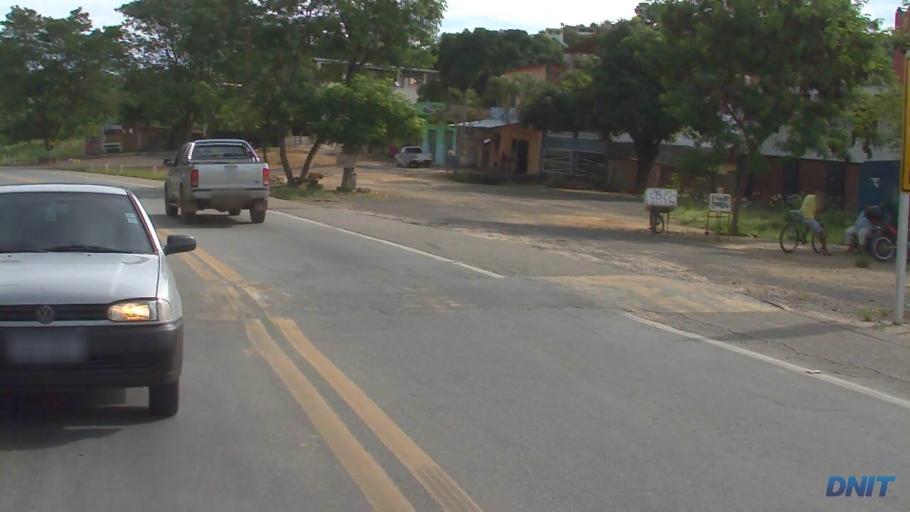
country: BR
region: Minas Gerais
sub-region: Belo Oriente
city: Belo Oriente
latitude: -19.2305
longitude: -42.3272
